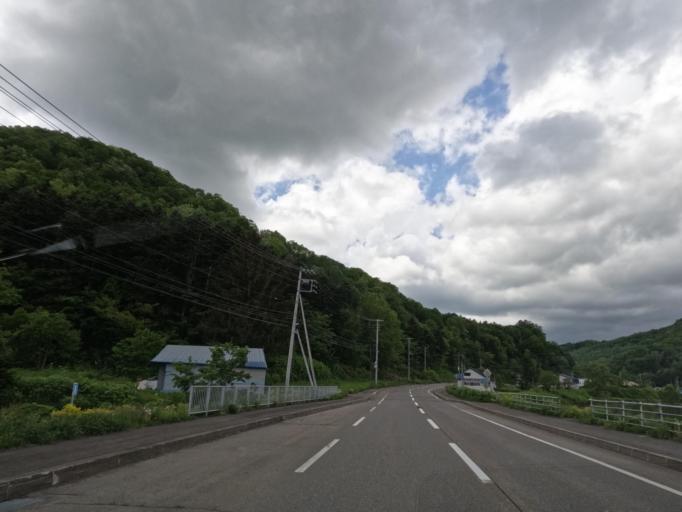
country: JP
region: Hokkaido
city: Takikawa
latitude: 43.5907
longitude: 141.7317
